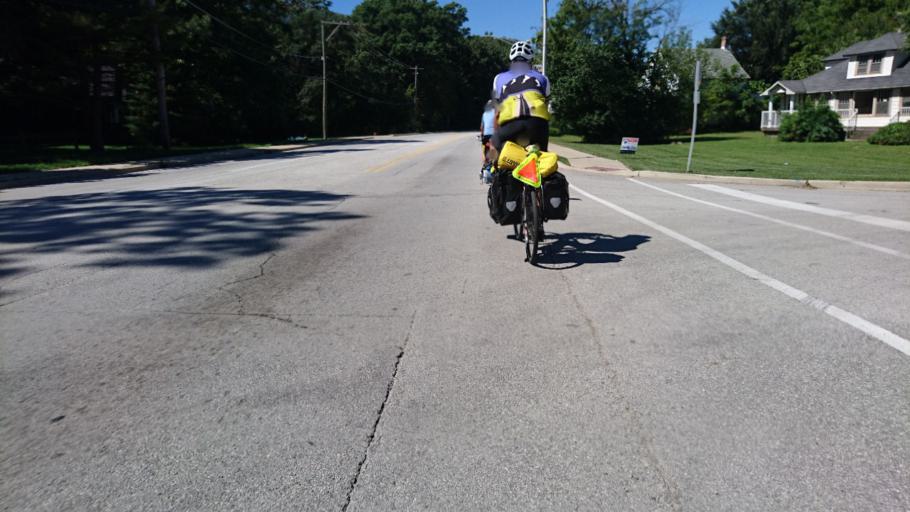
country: US
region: Illinois
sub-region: Cook County
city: Glenwood
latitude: 41.5449
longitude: -87.6158
